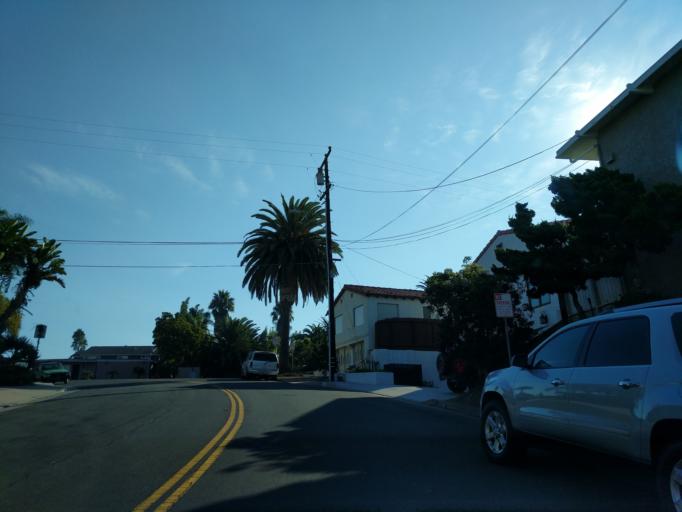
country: US
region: California
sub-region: Orange County
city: San Clemente
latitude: 33.4253
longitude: -117.6236
